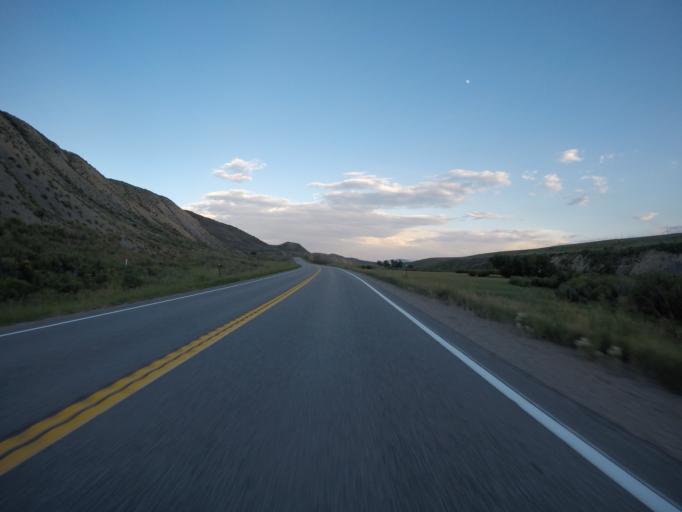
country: US
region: Colorado
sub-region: Grand County
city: Kremmling
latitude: 40.2705
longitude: -106.4670
